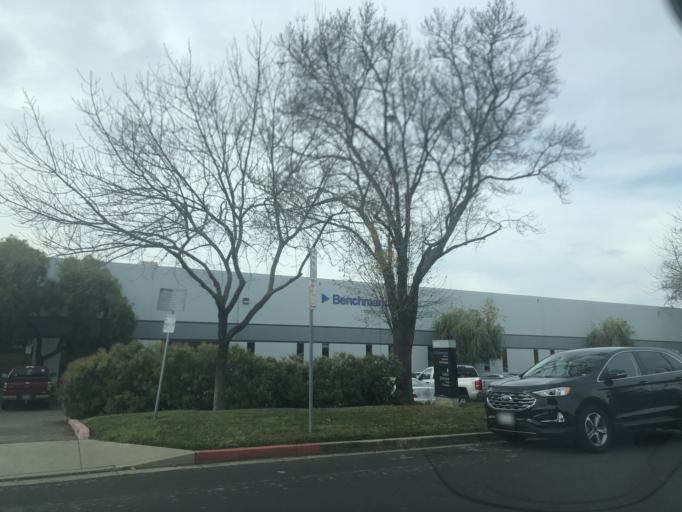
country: US
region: California
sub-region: Contra Costa County
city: Concord
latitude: 38.0097
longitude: -122.0307
